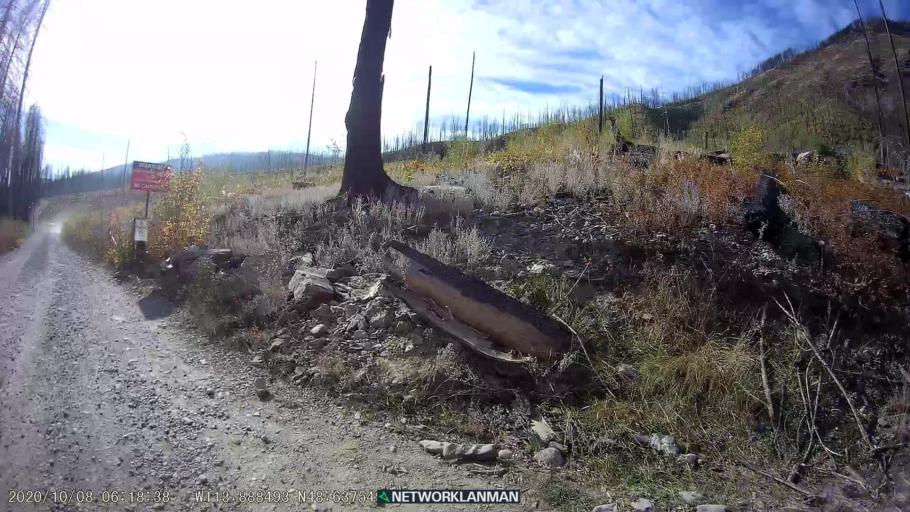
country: US
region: Montana
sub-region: Flathead County
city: Columbia Falls
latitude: 48.6375
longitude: -113.8886
